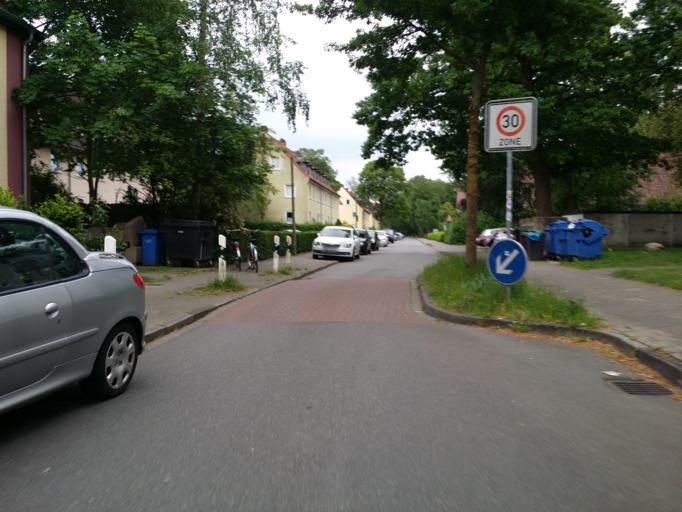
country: DE
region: Lower Saxony
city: Delmenhorst
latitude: 53.0357
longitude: 8.6384
